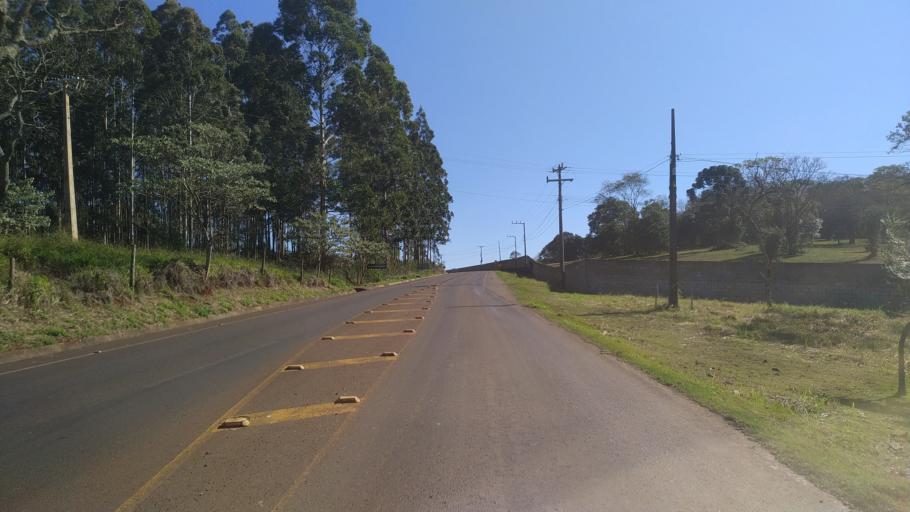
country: BR
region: Santa Catarina
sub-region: Chapeco
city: Chapeco
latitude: -27.1599
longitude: -52.6063
